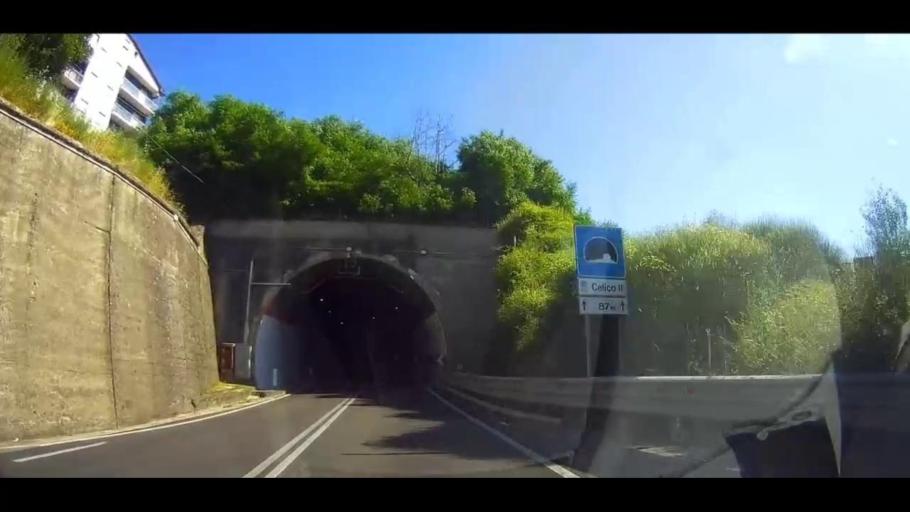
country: IT
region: Calabria
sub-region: Provincia di Cosenza
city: Celico
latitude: 39.3132
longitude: 16.3388
